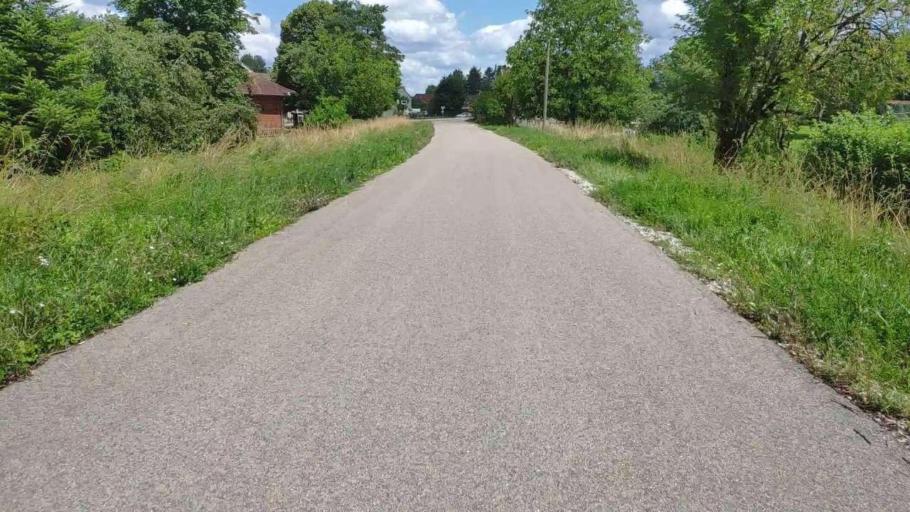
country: FR
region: Franche-Comte
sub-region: Departement du Jura
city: Bletterans
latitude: 46.8452
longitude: 5.4815
